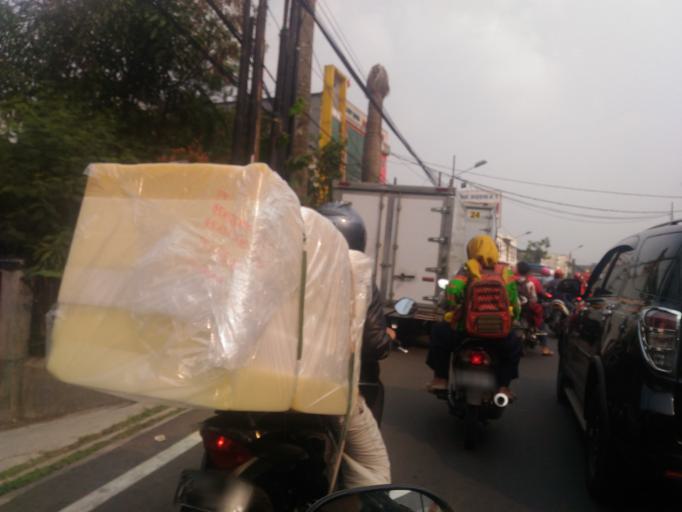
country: ID
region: West Java
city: Caringin
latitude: -6.6467
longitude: 106.8423
